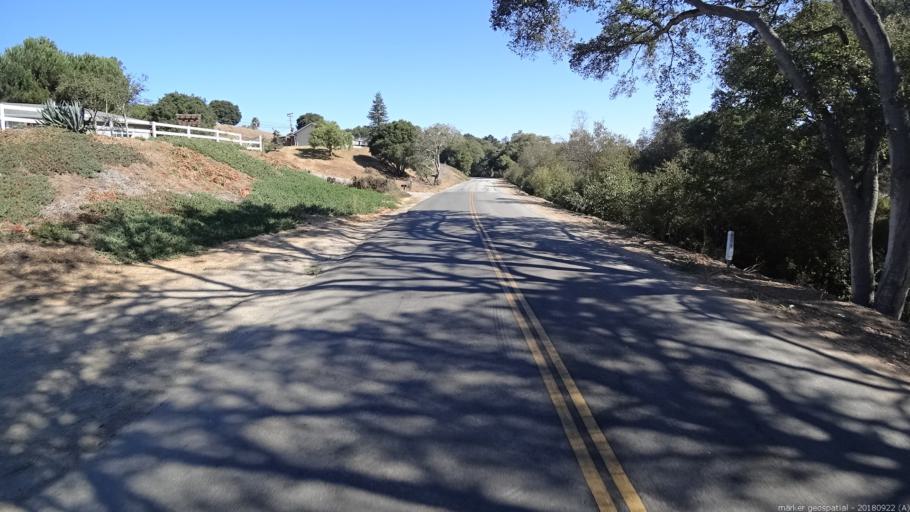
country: US
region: California
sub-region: Monterey County
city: Prunedale
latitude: 36.8063
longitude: -121.6498
